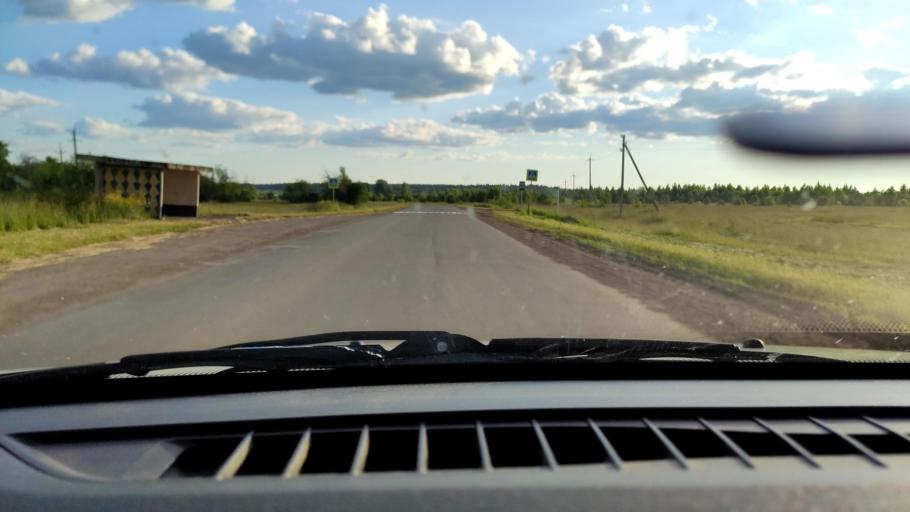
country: RU
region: Perm
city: Uinskoye
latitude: 57.0995
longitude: 56.6487
